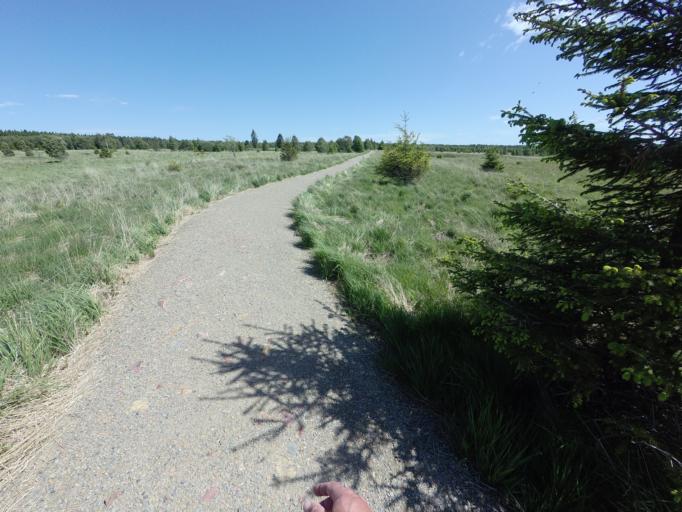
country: BE
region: Wallonia
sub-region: Province de Liege
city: Malmedy
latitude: 50.5065
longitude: 6.0669
